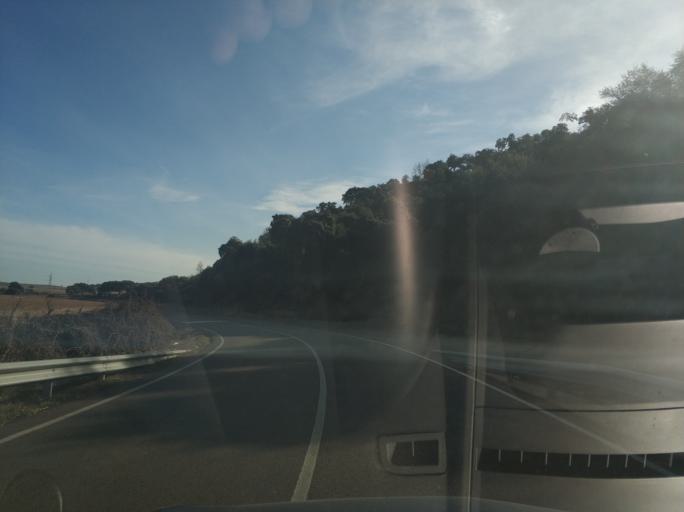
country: ES
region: Castille and Leon
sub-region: Provincia de Salamanca
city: Carrascal de Barregas
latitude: 40.9919
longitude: -5.7332
